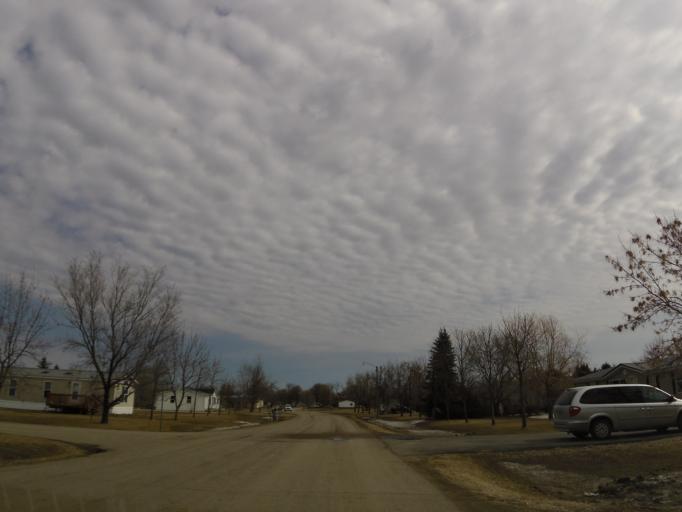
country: US
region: North Dakota
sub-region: Walsh County
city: Grafton
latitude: 48.2934
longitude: -97.3799
